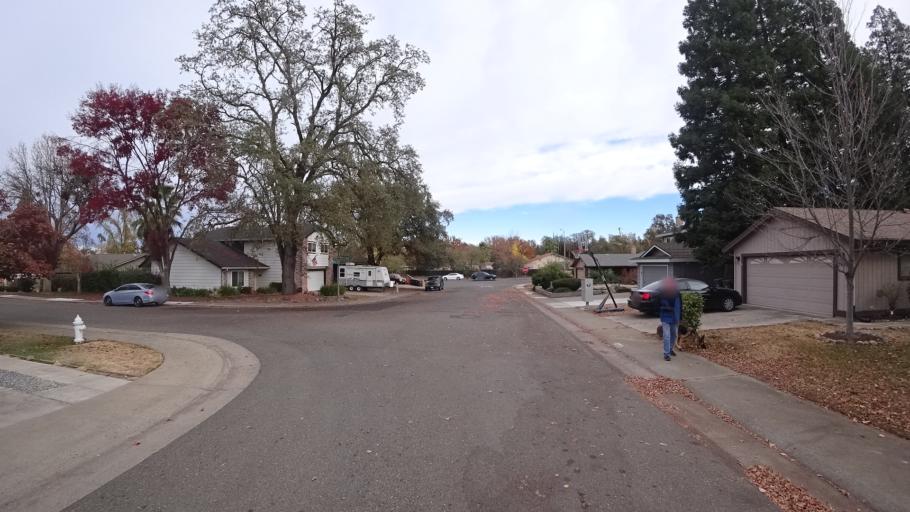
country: US
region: California
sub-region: Sacramento County
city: Citrus Heights
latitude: 38.7044
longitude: -121.2633
